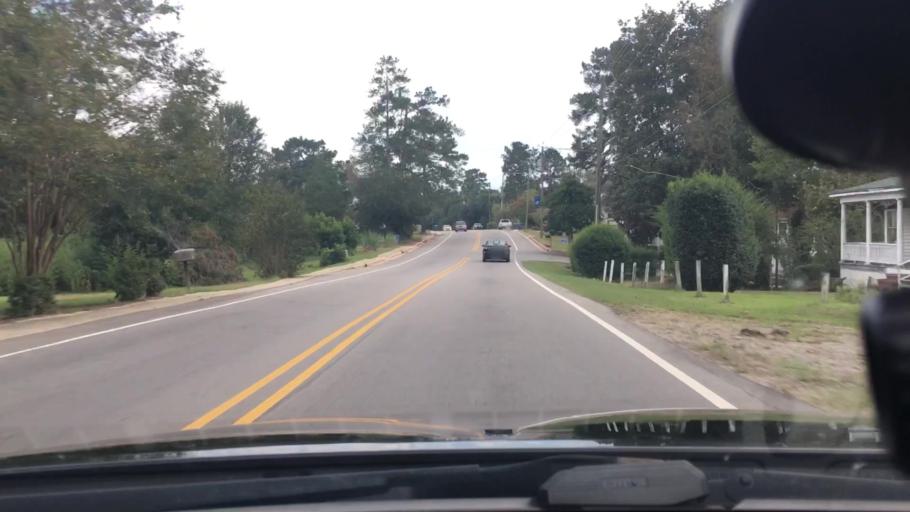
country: US
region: North Carolina
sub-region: Moore County
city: Carthage
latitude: 35.3532
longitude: -79.4230
